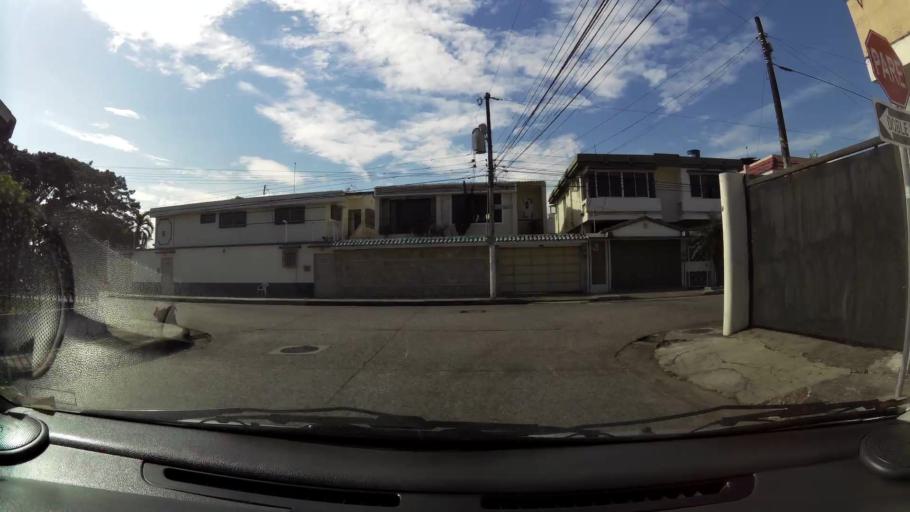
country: EC
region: Guayas
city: Guayaquil
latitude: -2.2255
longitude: -79.8936
